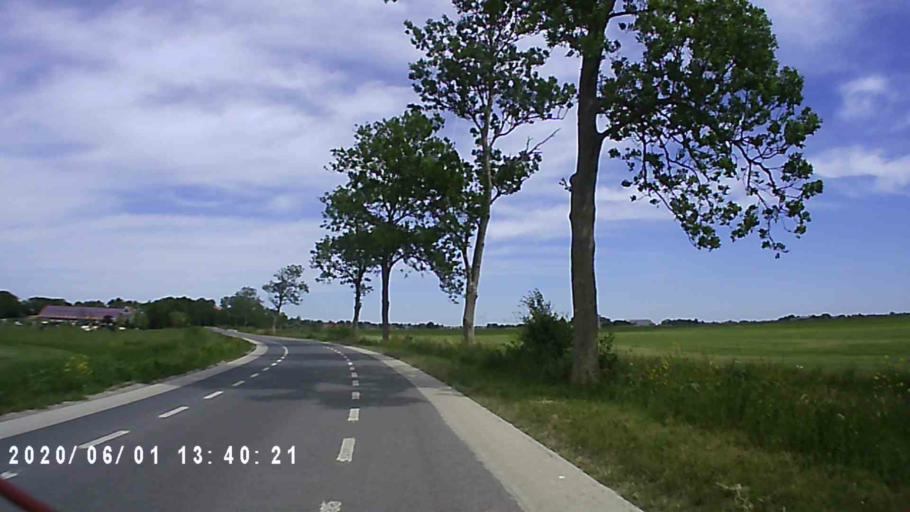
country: NL
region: Friesland
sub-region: Gemeente Littenseradiel
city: Wommels
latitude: 53.0888
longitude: 5.6027
